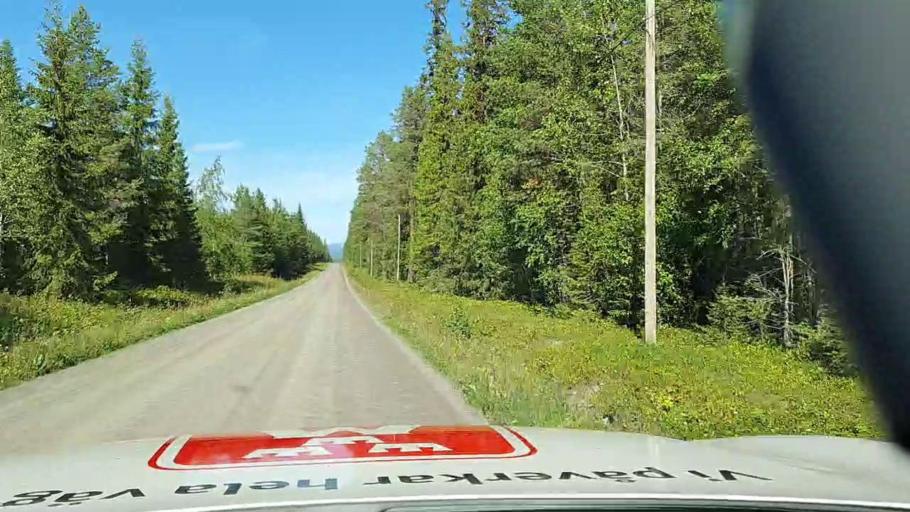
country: SE
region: Jaemtland
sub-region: Krokoms Kommun
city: Krokom
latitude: 63.6958
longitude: 14.6085
